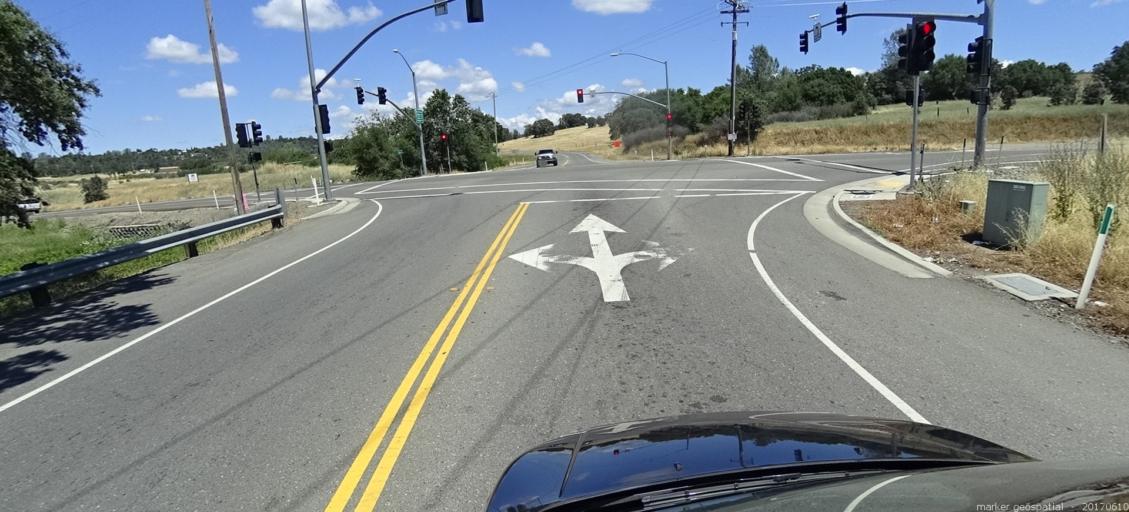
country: US
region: California
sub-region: Butte County
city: Oroville East
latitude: 39.5033
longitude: -121.4597
